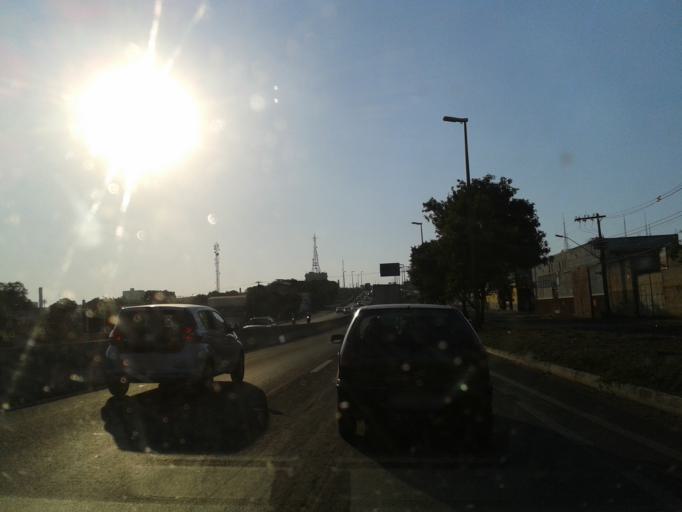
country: BR
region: Minas Gerais
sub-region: Uberlandia
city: Uberlandia
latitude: -18.8931
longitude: -48.2520
